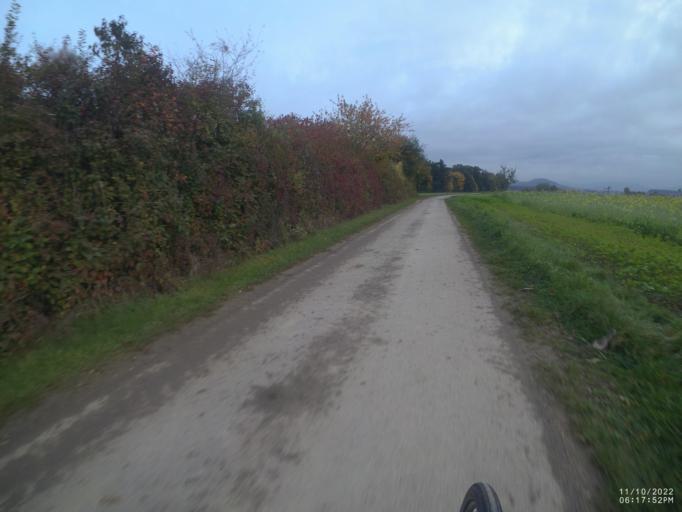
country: DE
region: Baden-Wuerttemberg
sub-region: Regierungsbezirk Stuttgart
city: Uhingen
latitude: 48.6830
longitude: 9.5924
